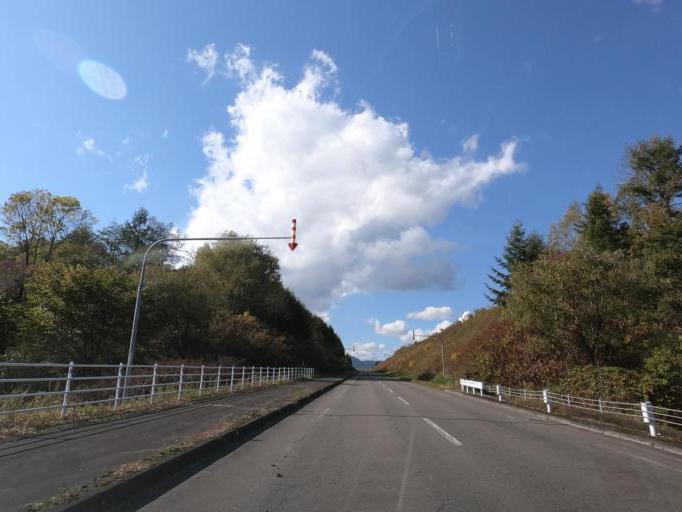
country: JP
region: Hokkaido
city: Otofuke
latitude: 43.2395
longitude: 143.2657
